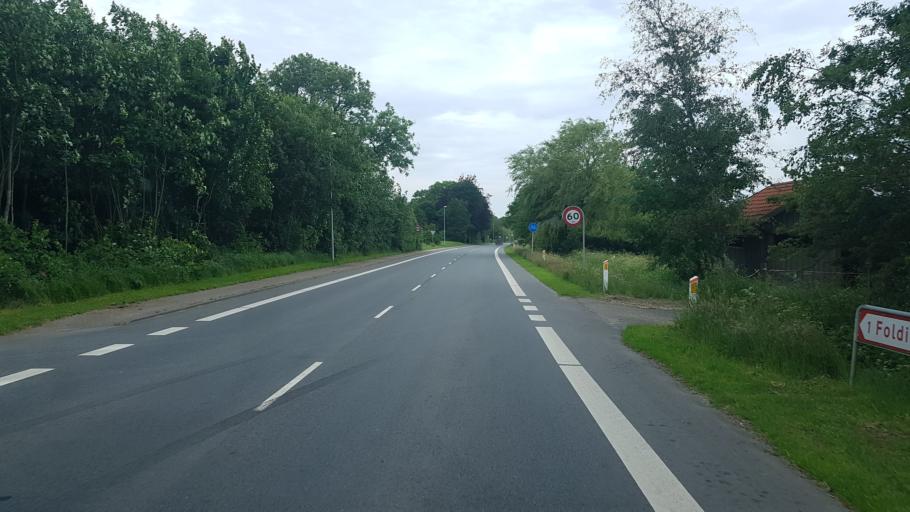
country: DK
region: South Denmark
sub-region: Vejen Kommune
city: Brorup
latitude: 55.4310
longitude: 9.0128
